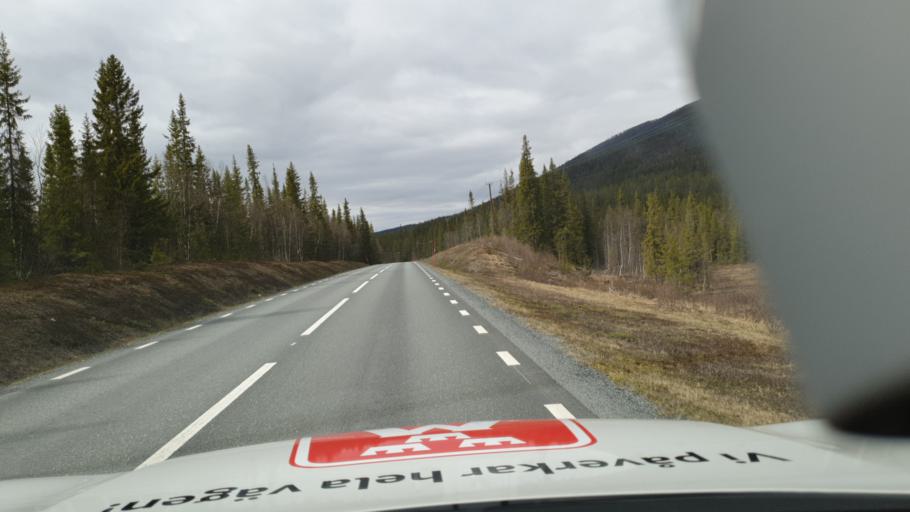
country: SE
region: Vaesterbotten
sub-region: Vilhelmina Kommun
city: Sjoberg
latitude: 65.5182
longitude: 15.6407
